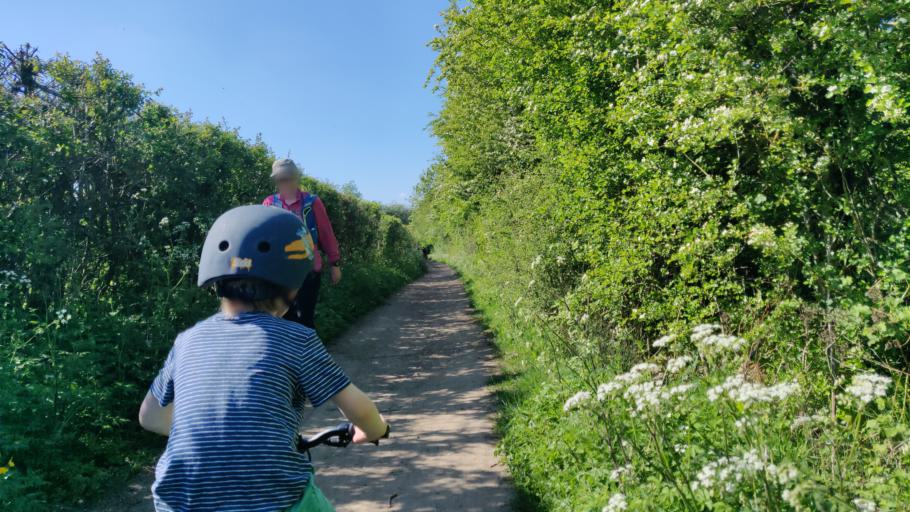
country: GB
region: England
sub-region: West Sussex
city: Southwater
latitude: 51.0584
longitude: -0.3818
